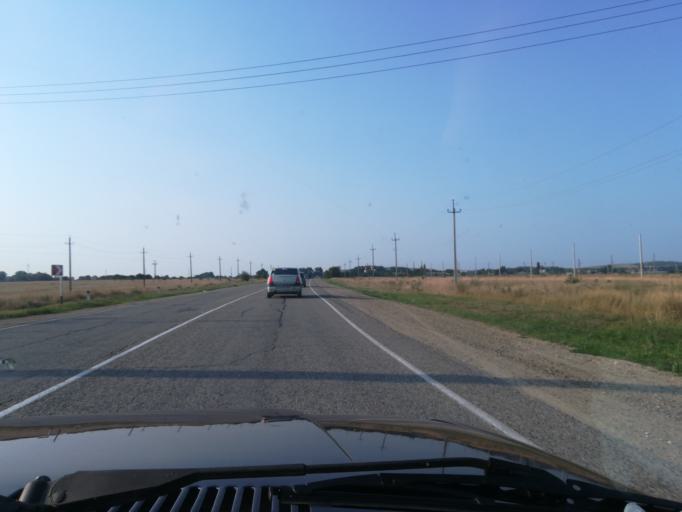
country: RU
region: Krasnodarskiy
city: Yurovka
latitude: 45.1051
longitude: 37.4219
